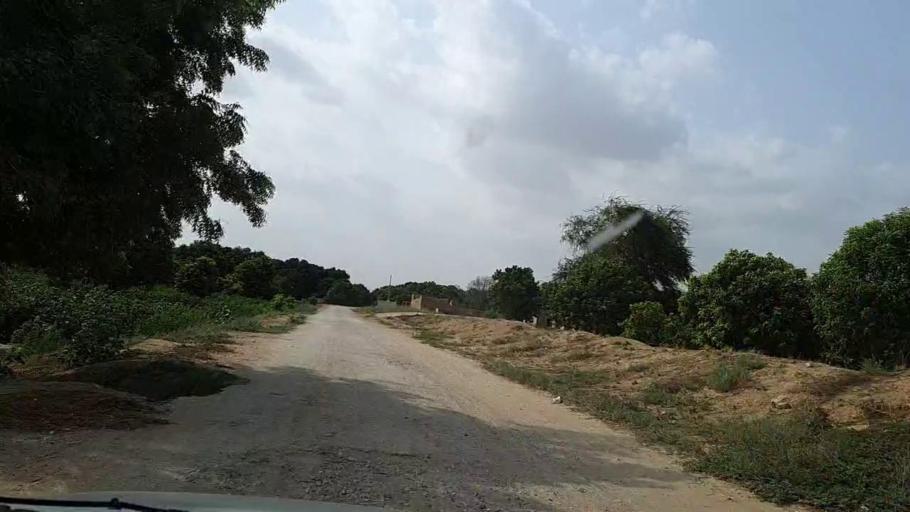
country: PK
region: Sindh
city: Kotri
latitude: 25.2480
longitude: 68.2603
